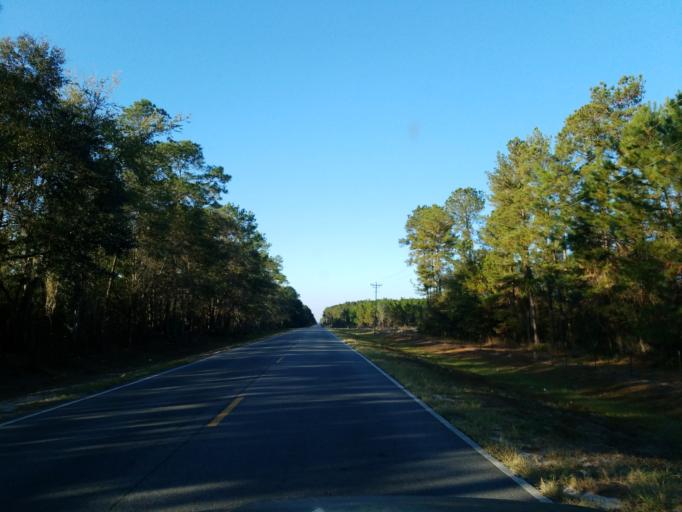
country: US
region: Georgia
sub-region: Lanier County
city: Lakeland
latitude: 31.0663
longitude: -83.0722
